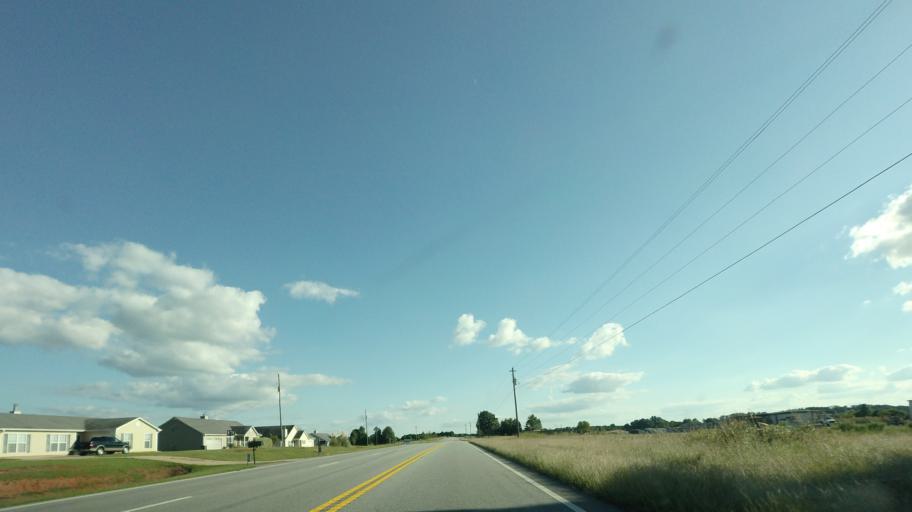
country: US
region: Georgia
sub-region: Upson County
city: Thomaston
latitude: 32.9406
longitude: -84.2573
